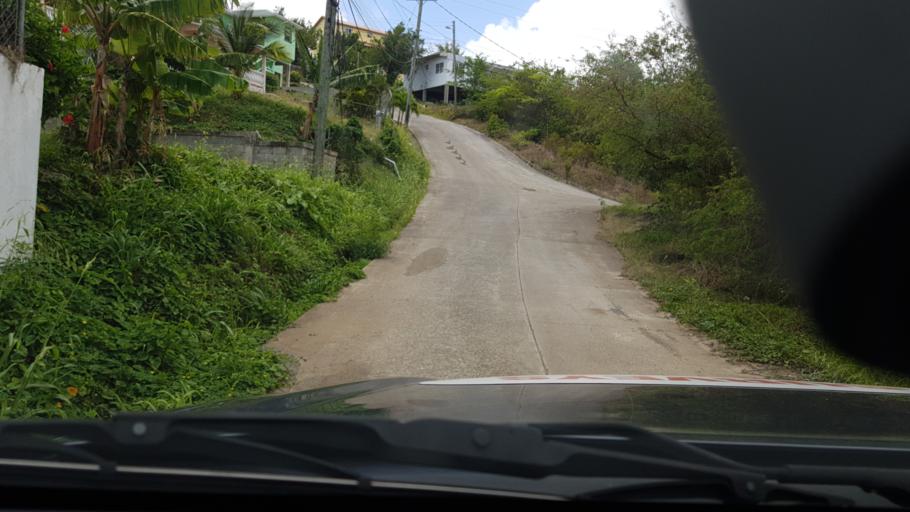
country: LC
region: Gros-Islet
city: Gros Islet
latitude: 14.0666
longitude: -60.9302
